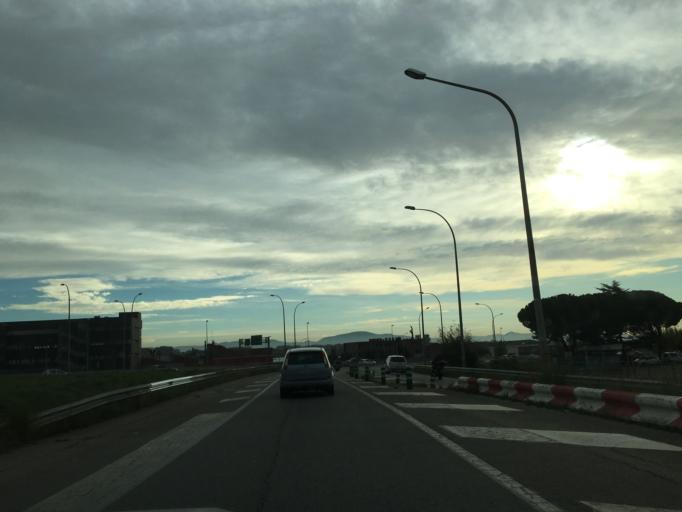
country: ES
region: Catalonia
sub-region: Provincia de Barcelona
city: Sant Quirze del Valles
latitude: 41.5286
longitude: 2.0926
